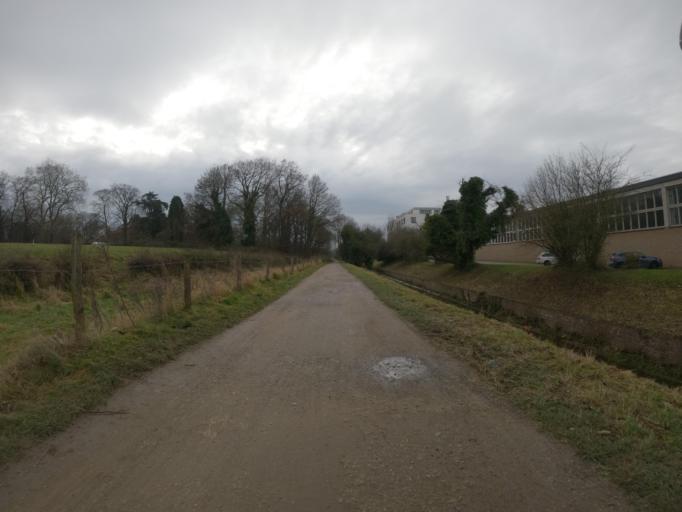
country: DE
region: North Rhine-Westphalia
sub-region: Regierungsbezirk Koln
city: Aachen
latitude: 50.7862
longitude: 6.1168
